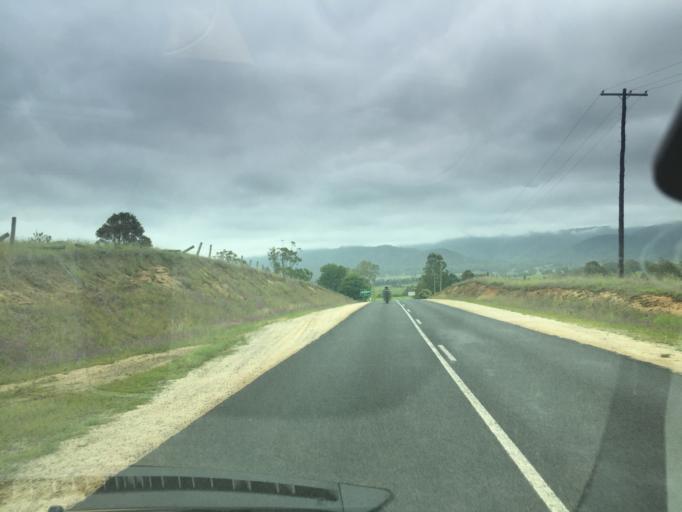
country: AU
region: New South Wales
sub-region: Bega Valley
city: Bega
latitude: -36.6469
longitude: 149.5847
